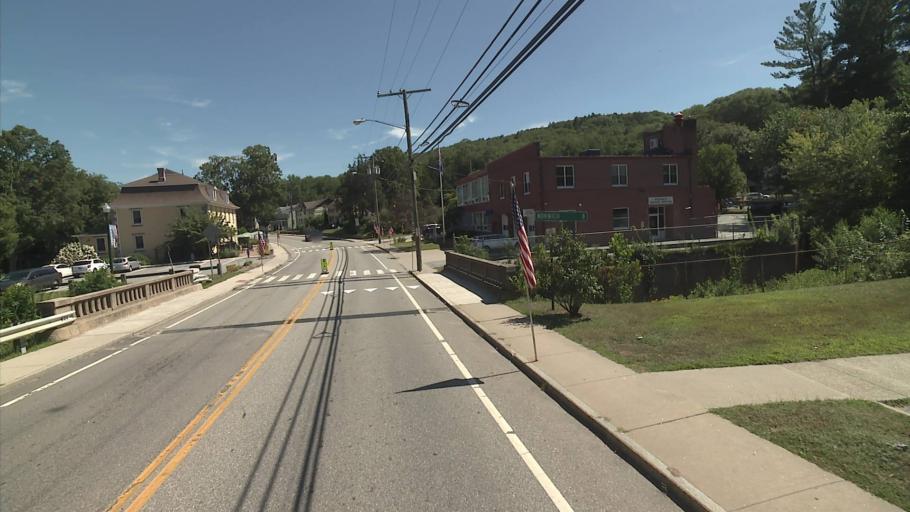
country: US
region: Connecticut
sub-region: New London County
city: Baltic
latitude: 41.6168
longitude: -72.0846
